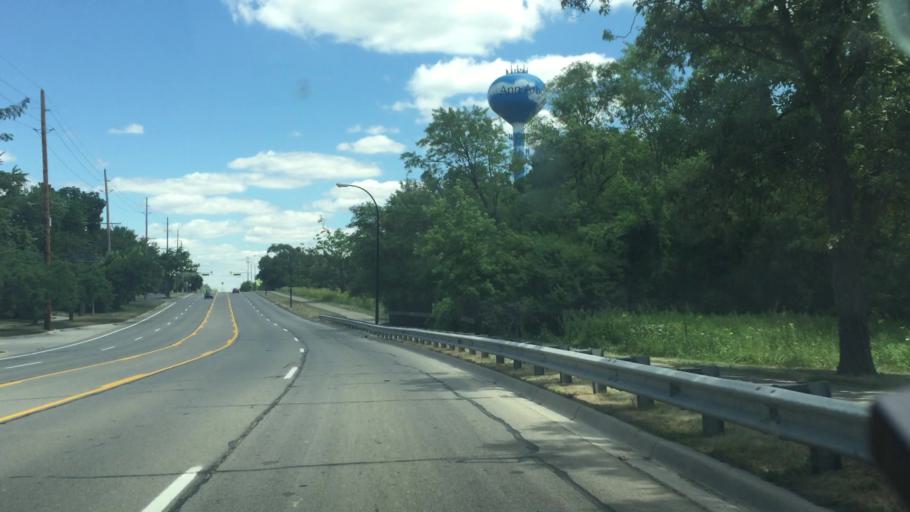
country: US
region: Michigan
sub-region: Washtenaw County
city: Ann Arbor
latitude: 42.3027
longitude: -83.7013
